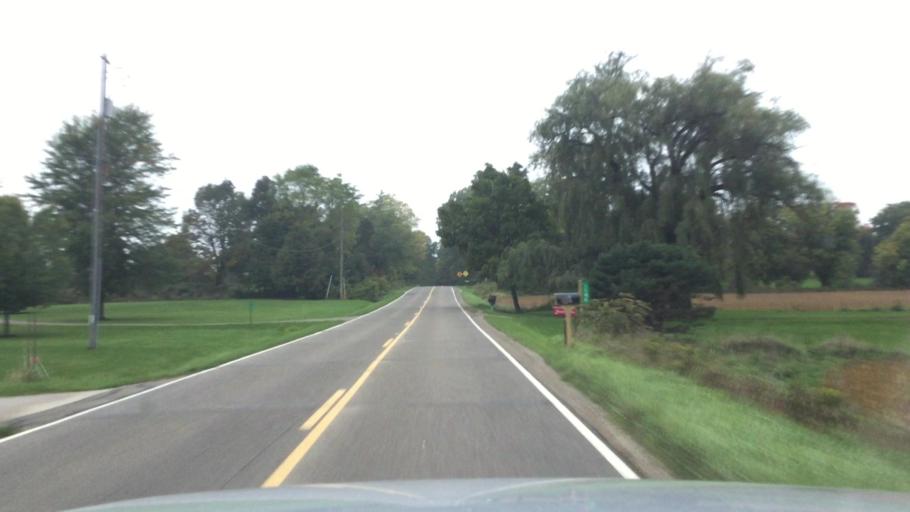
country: US
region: Michigan
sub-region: Shiawassee County
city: Corunna
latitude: 42.9378
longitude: -84.1403
